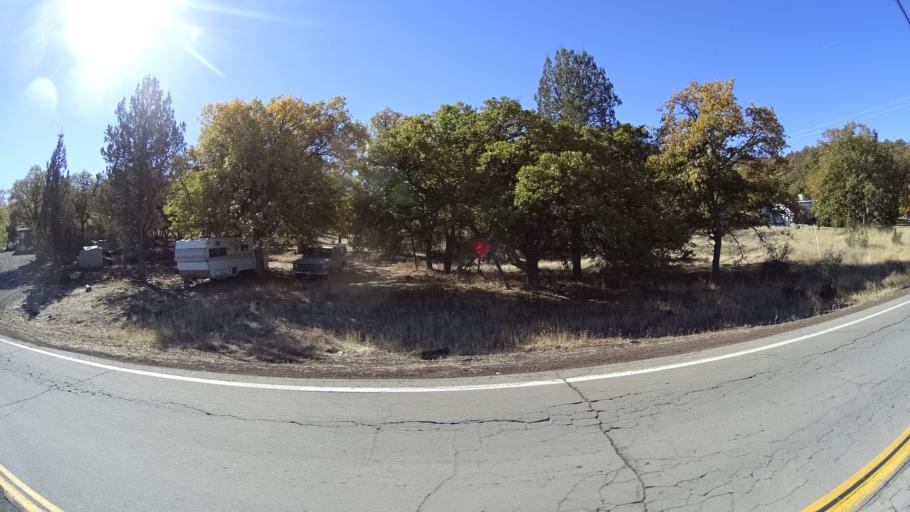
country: US
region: California
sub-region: Siskiyou County
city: Montague
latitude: 41.8867
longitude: -122.4896
